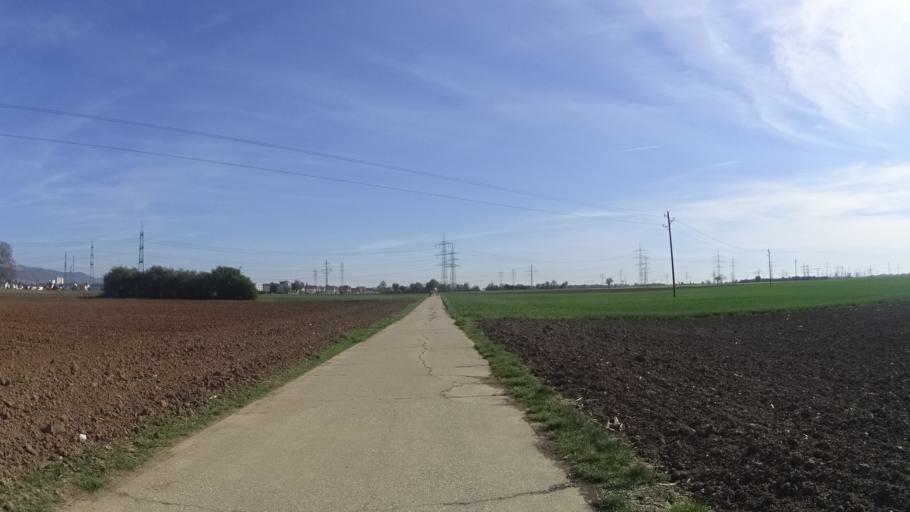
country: DE
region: Baden-Wuerttemberg
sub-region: Karlsruhe Region
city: Heddesheim
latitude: 49.5162
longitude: 8.5896
